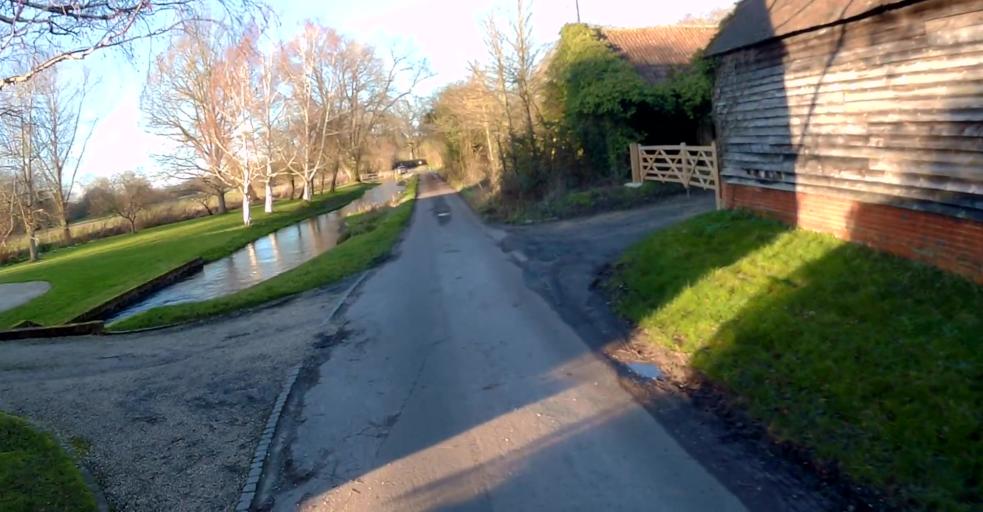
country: GB
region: England
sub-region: Hampshire
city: Hook
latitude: 51.3098
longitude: -1.0017
